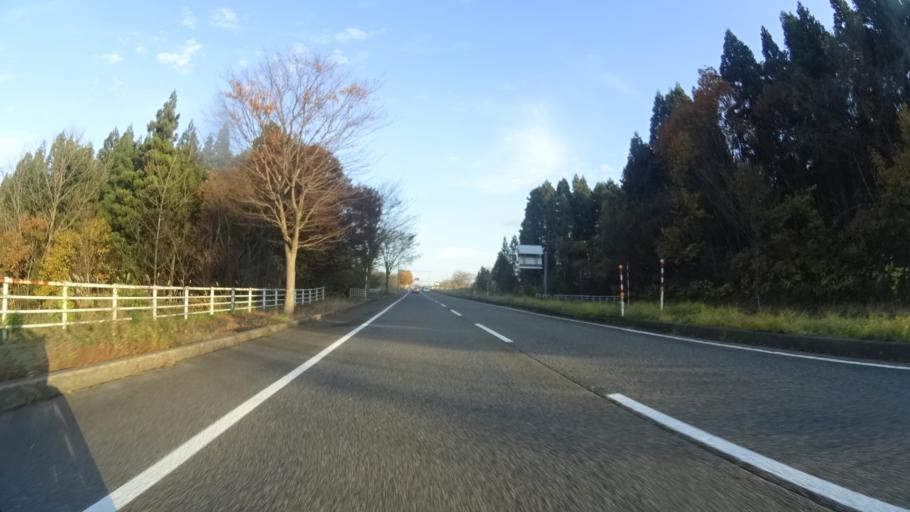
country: JP
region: Niigata
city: Nagaoka
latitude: 37.4504
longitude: 138.7634
